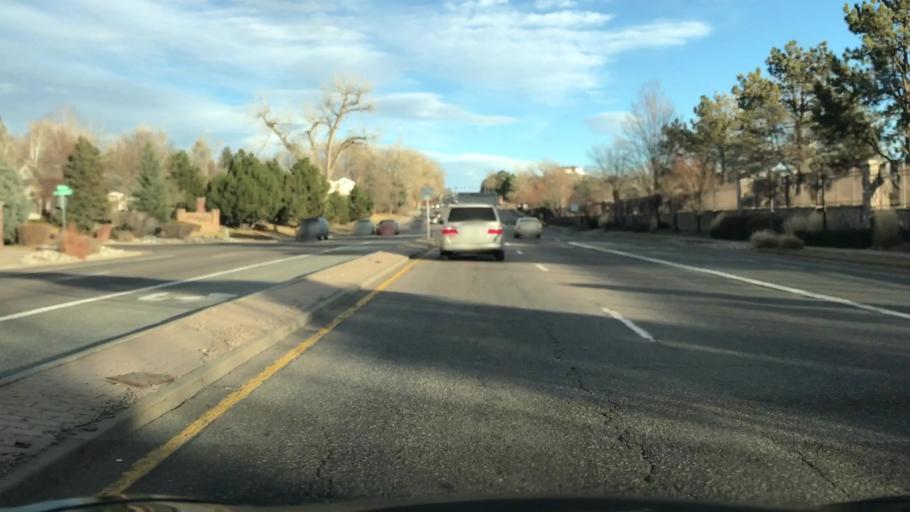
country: US
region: Colorado
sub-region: Arapahoe County
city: Glendale
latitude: 39.6747
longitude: -104.8840
